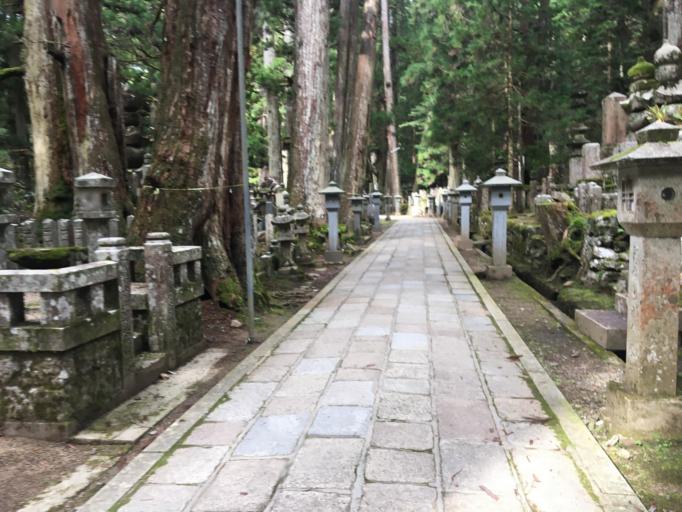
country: JP
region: Wakayama
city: Koya
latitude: 34.2175
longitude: 135.6003
